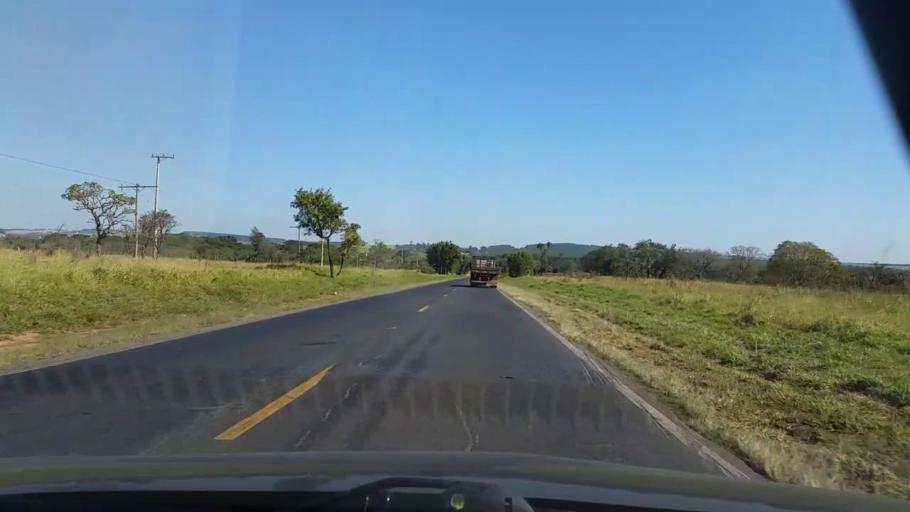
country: BR
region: Sao Paulo
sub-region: Sao Manuel
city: Sao Manuel
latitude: -22.7980
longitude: -48.6621
